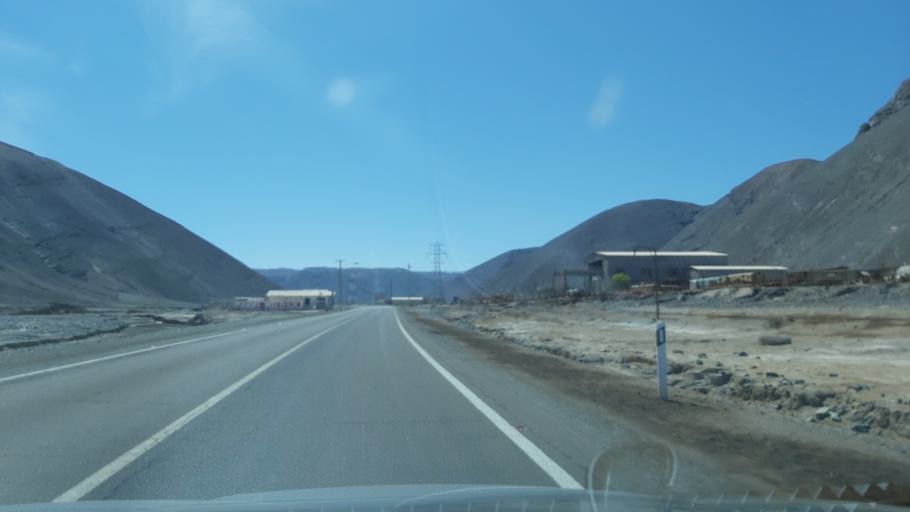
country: CL
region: Atacama
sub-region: Provincia de Chanaral
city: Diego de Almagro
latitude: -26.3337
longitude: -69.8256
